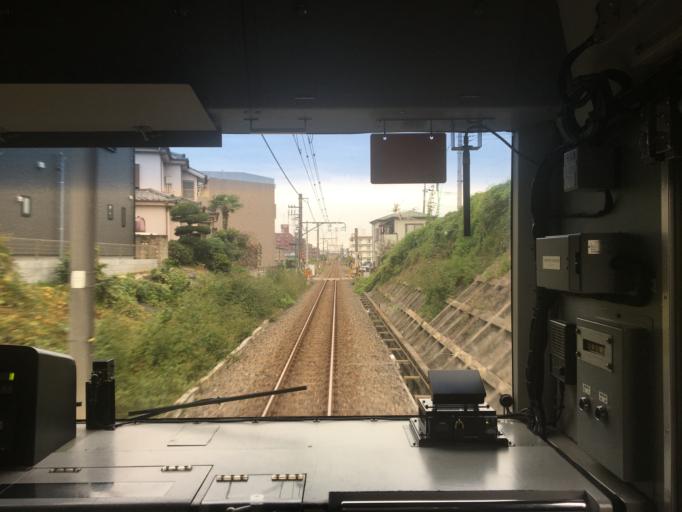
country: JP
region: Saitama
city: Kawagoe
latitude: 35.9145
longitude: 139.4742
